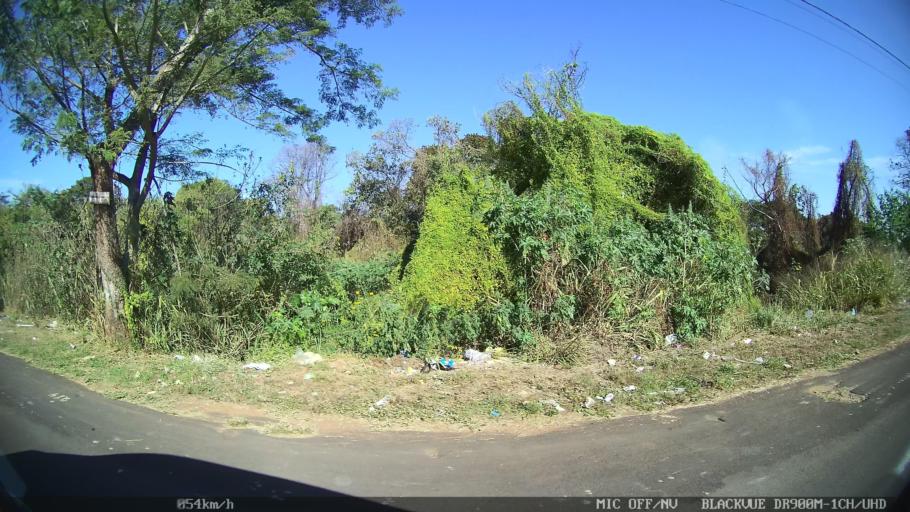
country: BR
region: Sao Paulo
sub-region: Franca
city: Franca
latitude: -20.4859
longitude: -47.4246
